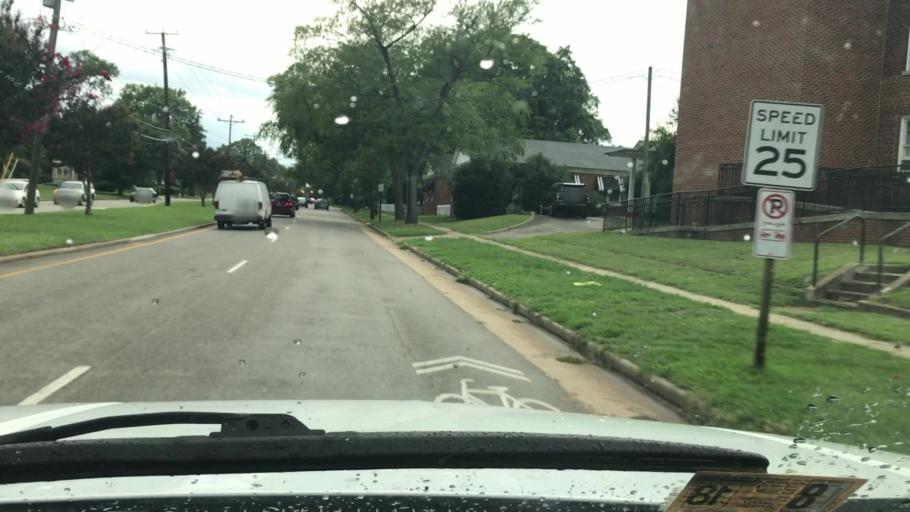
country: US
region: Virginia
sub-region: City of Richmond
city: Richmond
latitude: 37.5723
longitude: -77.4455
